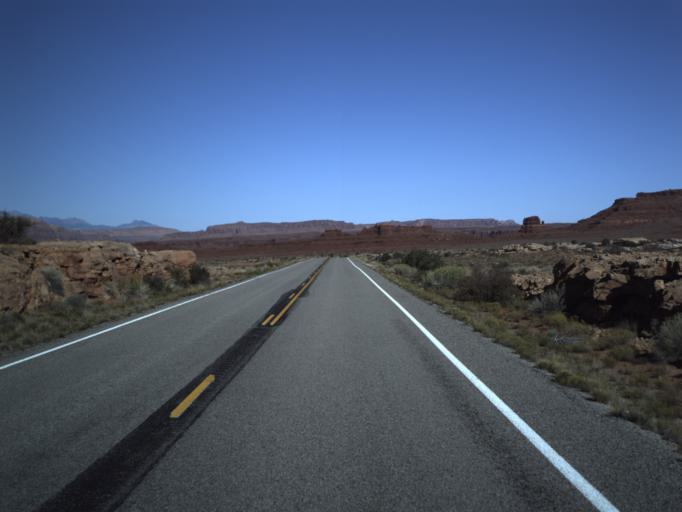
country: US
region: Utah
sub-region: San Juan County
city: Blanding
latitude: 37.8149
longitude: -110.3439
